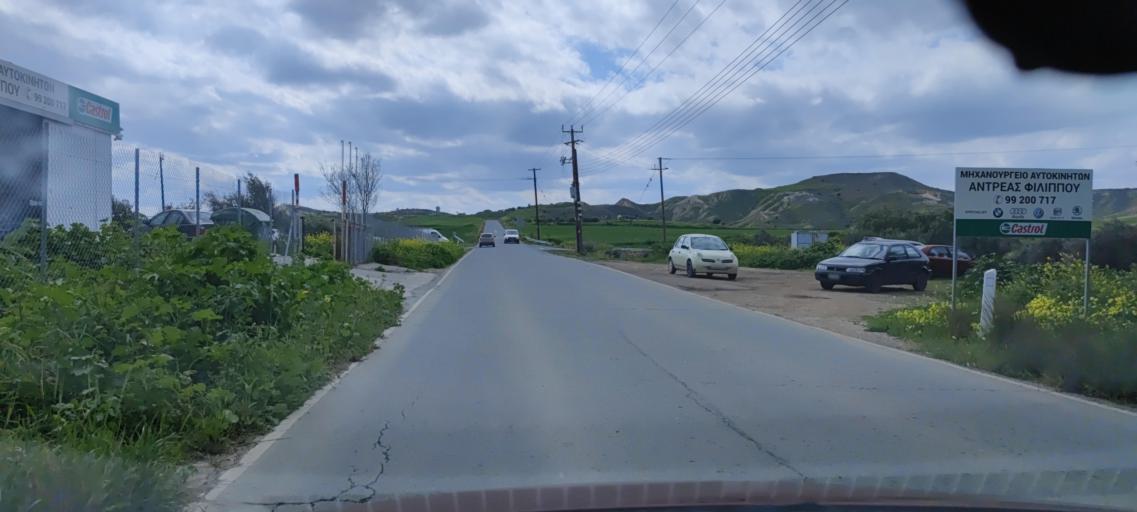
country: CY
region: Lefkosia
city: Tseri
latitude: 35.0390
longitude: 33.3156
